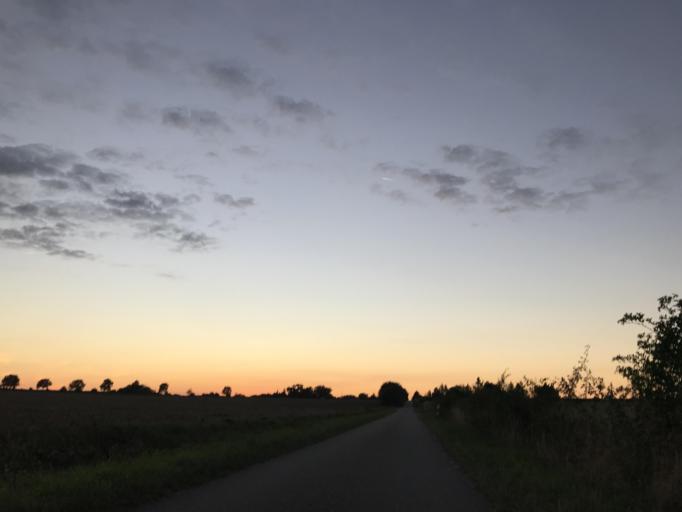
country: DE
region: Lower Saxony
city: Reinstorf
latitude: 53.2314
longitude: 10.5850
